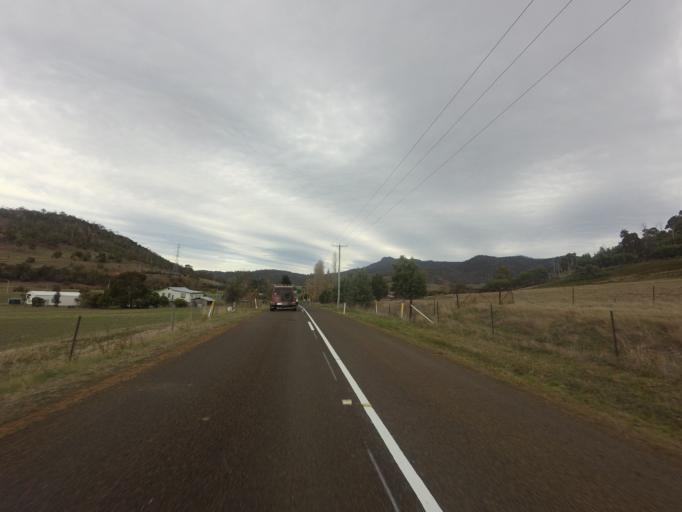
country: AU
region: Tasmania
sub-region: Brighton
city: Bridgewater
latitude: -42.6554
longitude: 147.1257
